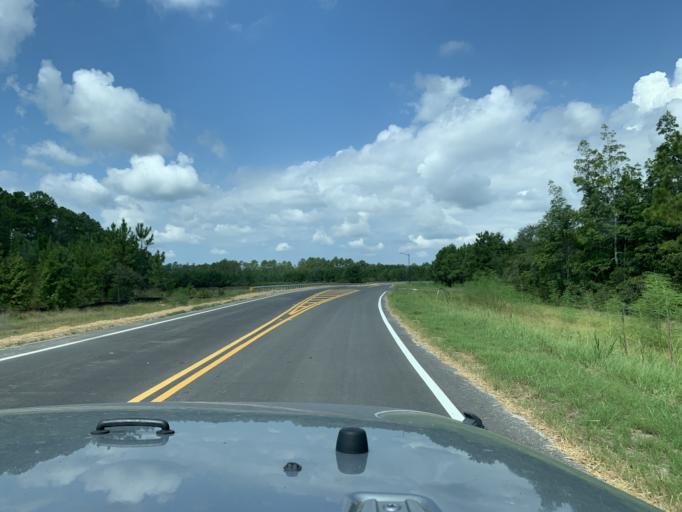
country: US
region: Georgia
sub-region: Chatham County
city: Bloomingdale
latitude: 32.0996
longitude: -81.3720
